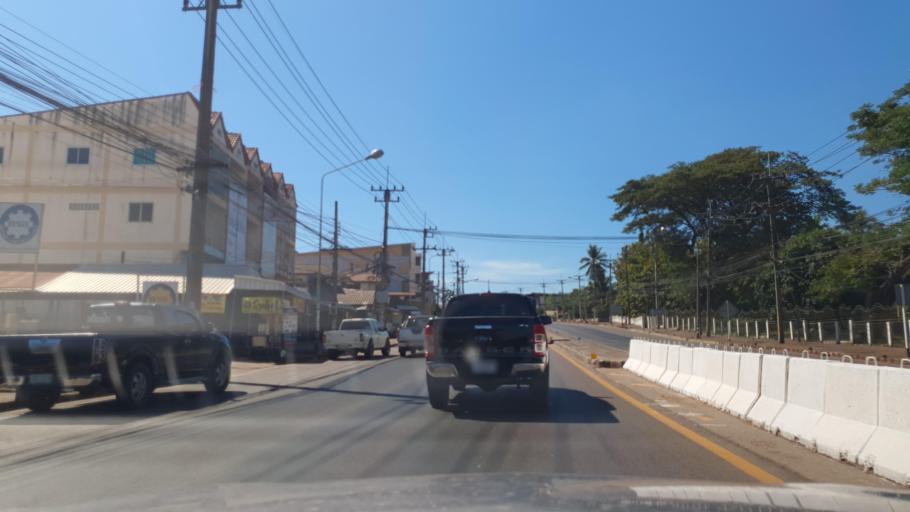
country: TH
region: Sakon Nakhon
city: Sakon Nakhon
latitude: 17.1894
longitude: 104.0940
